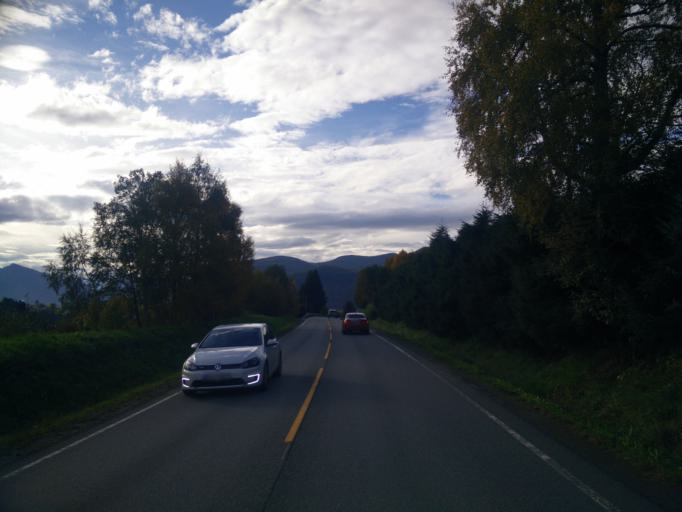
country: NO
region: More og Romsdal
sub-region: Vestnes
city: Vestnes
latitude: 62.6379
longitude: 7.0768
